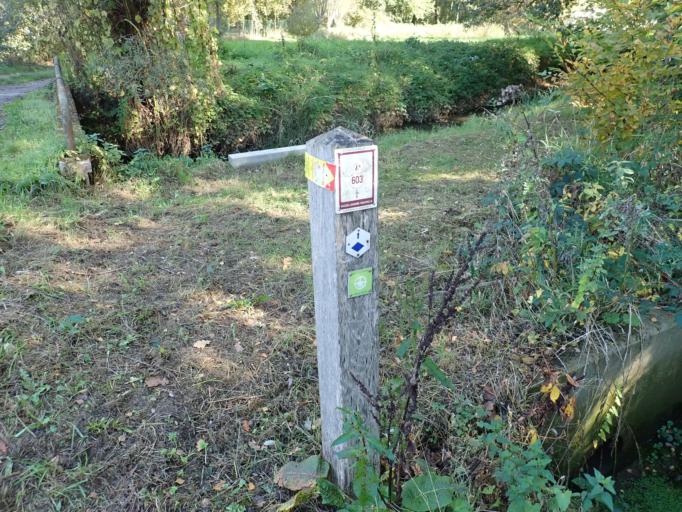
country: BE
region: Flanders
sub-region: Provincie Vlaams-Brabant
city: Holsbeek
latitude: 50.9325
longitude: 4.7513
